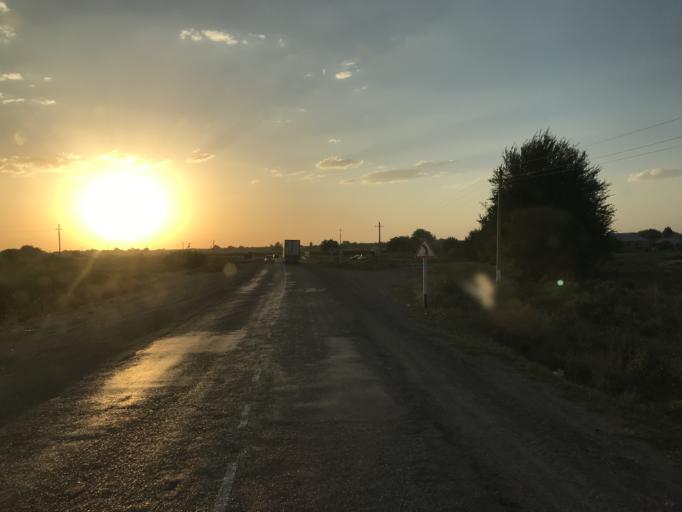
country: UZ
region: Toshkent
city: Yangiyul
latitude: 41.3738
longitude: 68.8271
